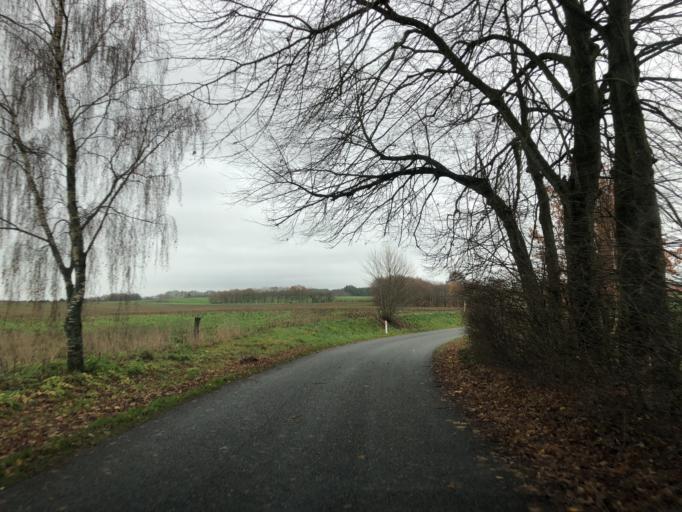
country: DK
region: Central Jutland
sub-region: Silkeborg Kommune
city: Virklund
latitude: 56.0691
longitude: 9.5227
